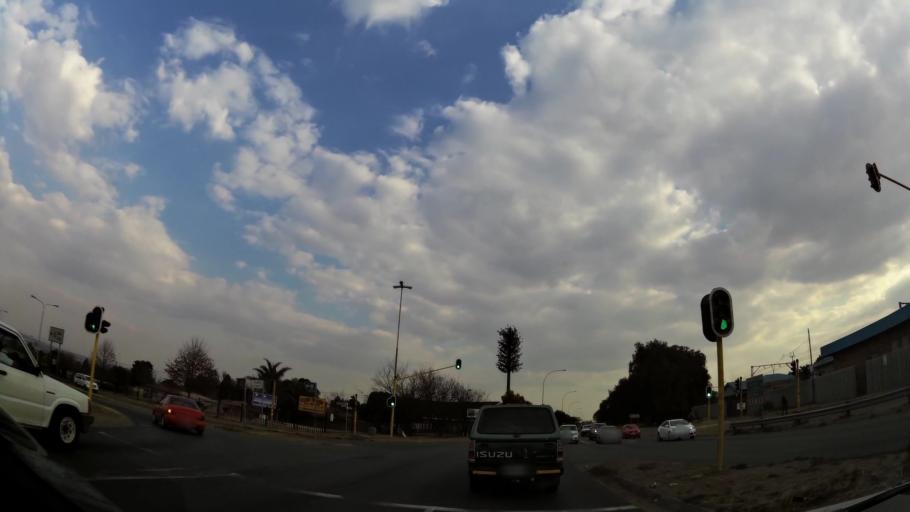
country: ZA
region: Gauteng
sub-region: Ekurhuleni Metropolitan Municipality
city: Germiston
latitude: -26.2418
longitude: 28.1940
